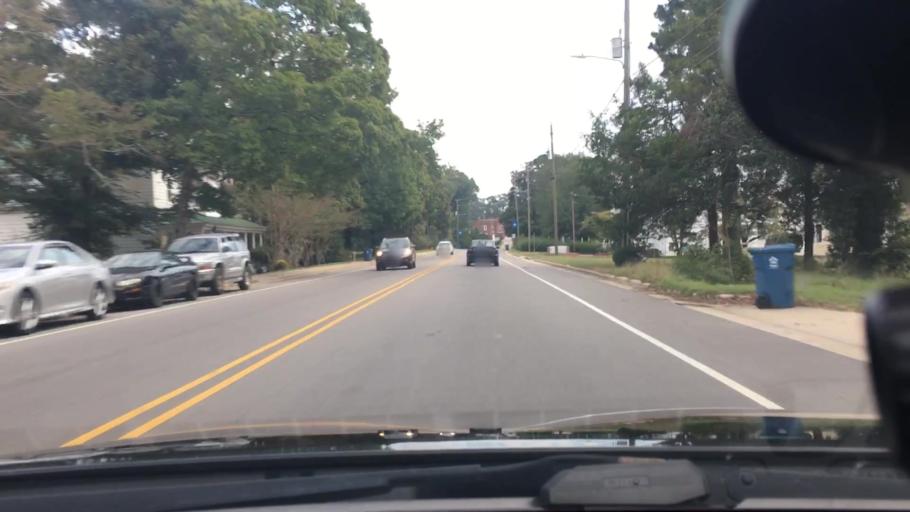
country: US
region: North Carolina
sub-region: Moore County
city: Carthage
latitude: 35.3499
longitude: -79.4206
